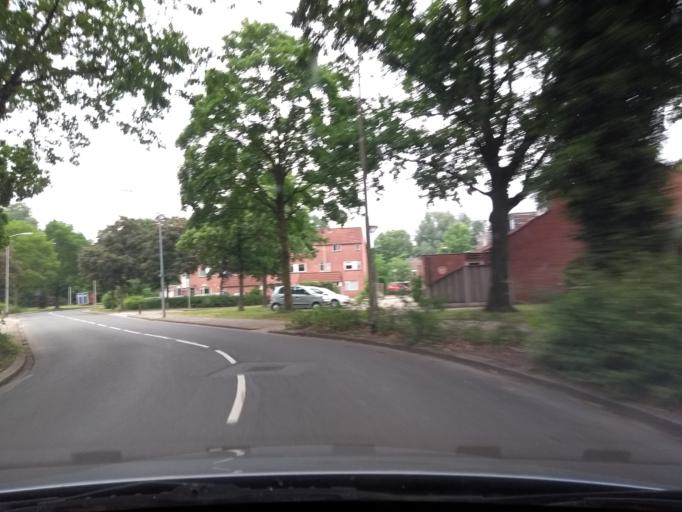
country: NL
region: Overijssel
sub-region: Gemeente Almelo
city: Almelo
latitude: 52.3384
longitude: 6.6298
